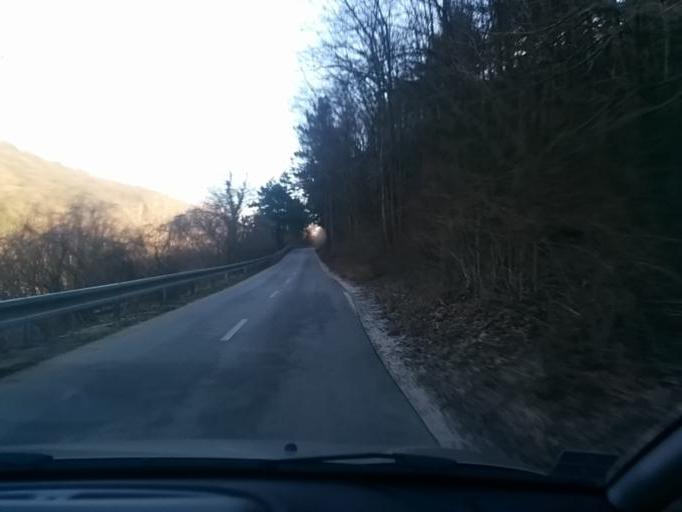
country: SK
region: Nitriansky
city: Cachtice
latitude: 48.7264
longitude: 17.7774
